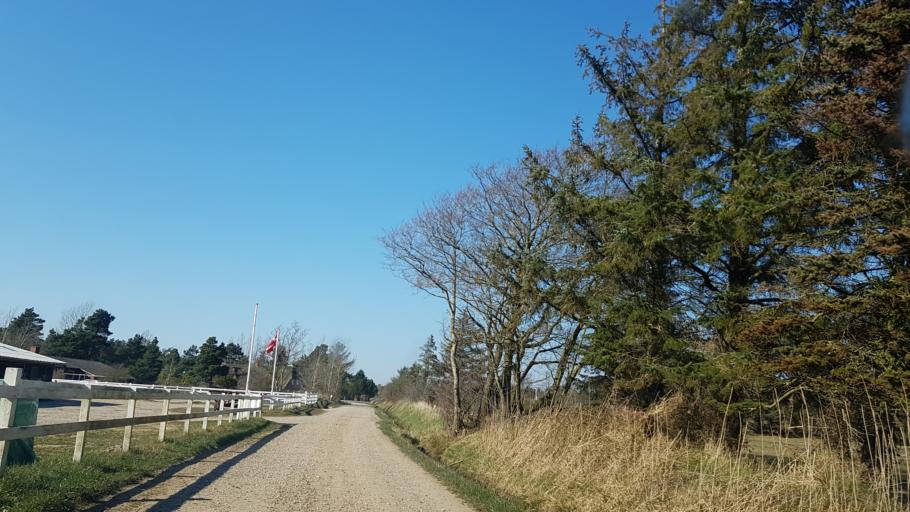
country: DE
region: Schleswig-Holstein
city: List
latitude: 55.0939
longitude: 8.5386
